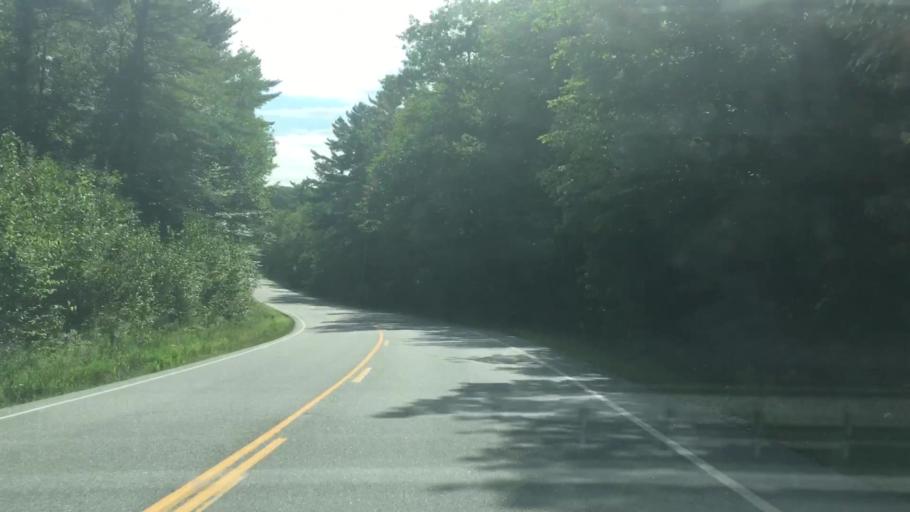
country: US
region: Maine
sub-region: Androscoggin County
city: Poland
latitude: 44.0213
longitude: -70.4402
